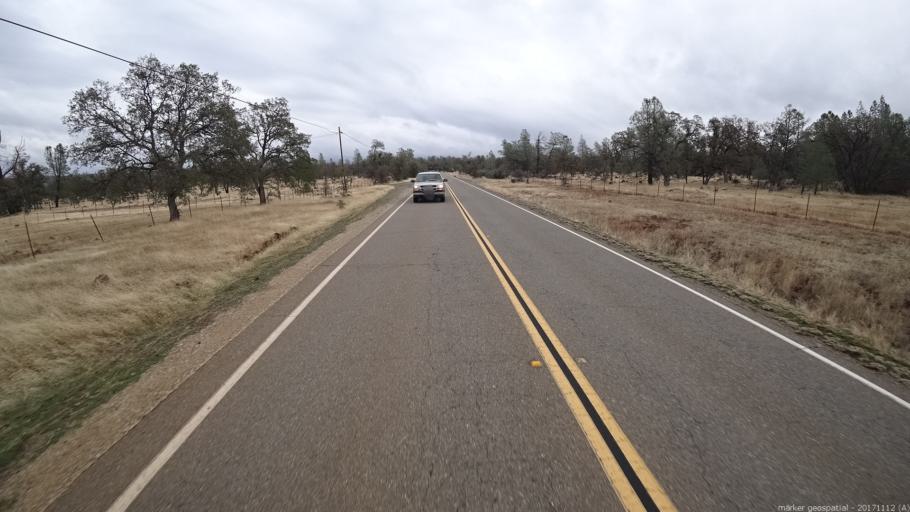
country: US
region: California
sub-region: Shasta County
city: Palo Cedro
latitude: 40.4811
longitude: -122.0866
